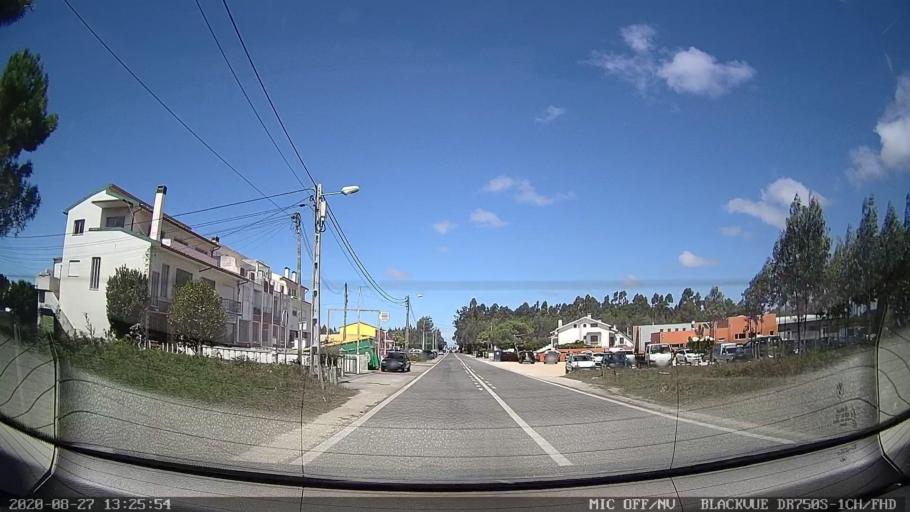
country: PT
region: Aveiro
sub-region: Vagos
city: Vagos
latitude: 40.5423
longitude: -8.6779
